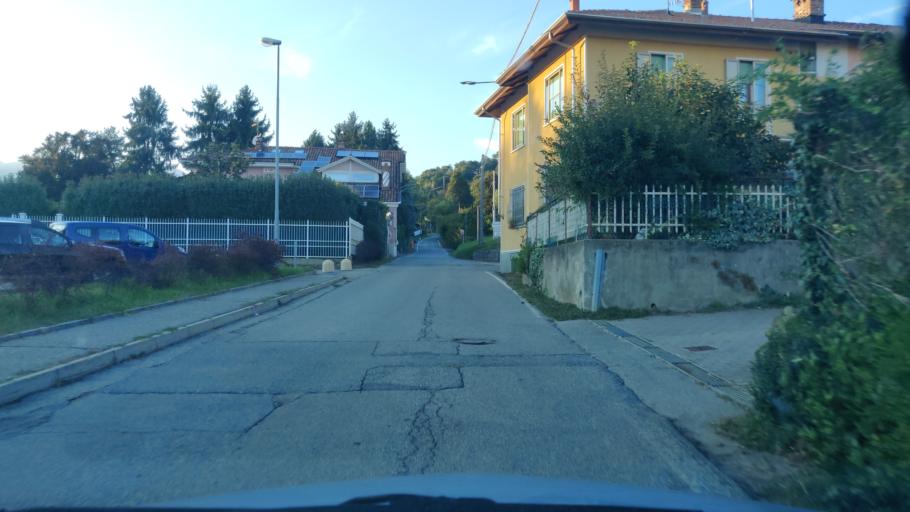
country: IT
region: Piedmont
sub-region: Provincia di Biella
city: Ronco Biellese
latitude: 45.5791
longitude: 8.0865
